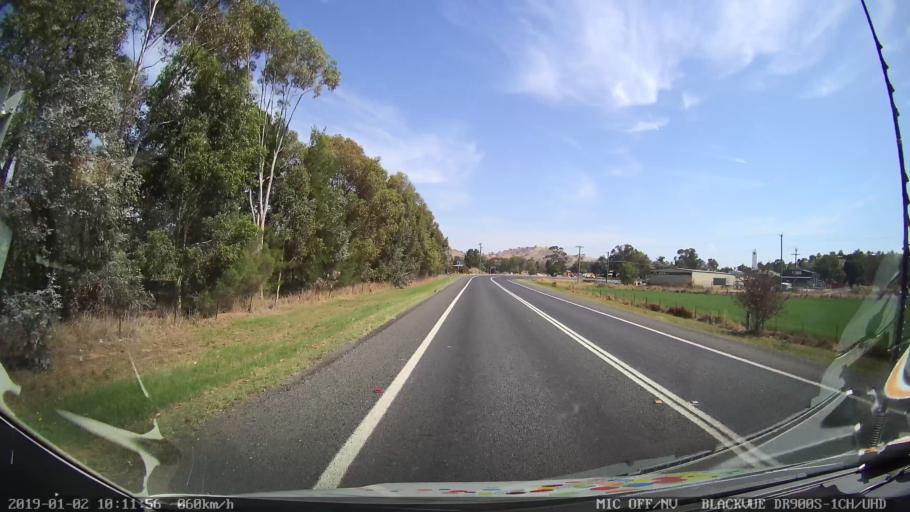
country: AU
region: New South Wales
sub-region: Gundagai
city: Gundagai
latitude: -35.0884
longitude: 148.0937
